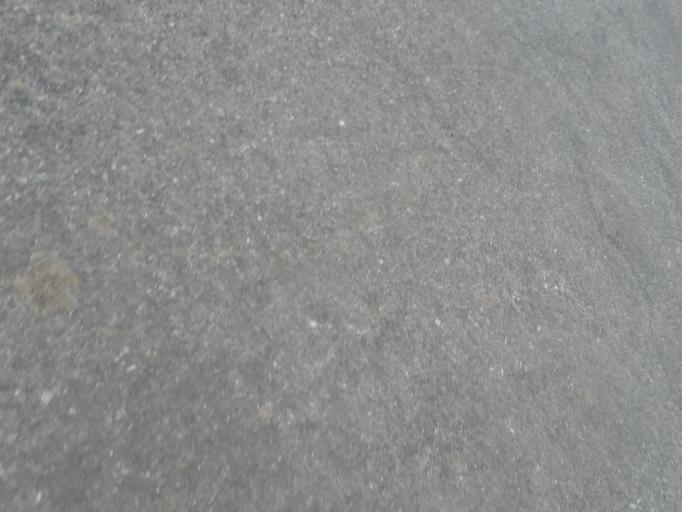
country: PT
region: Madeira
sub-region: Santana
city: Santana
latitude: 32.8226
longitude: -16.8859
